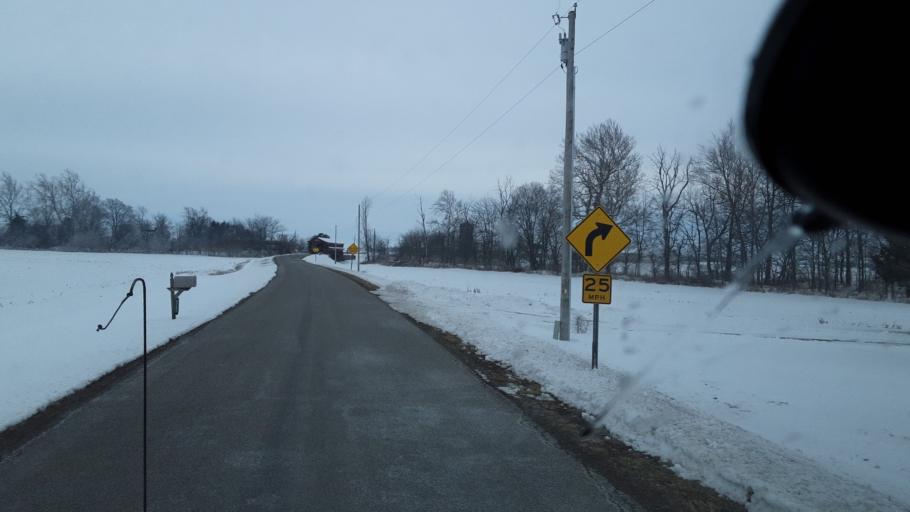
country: US
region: Ohio
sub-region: Union County
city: Marysville
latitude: 40.1183
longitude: -83.4247
